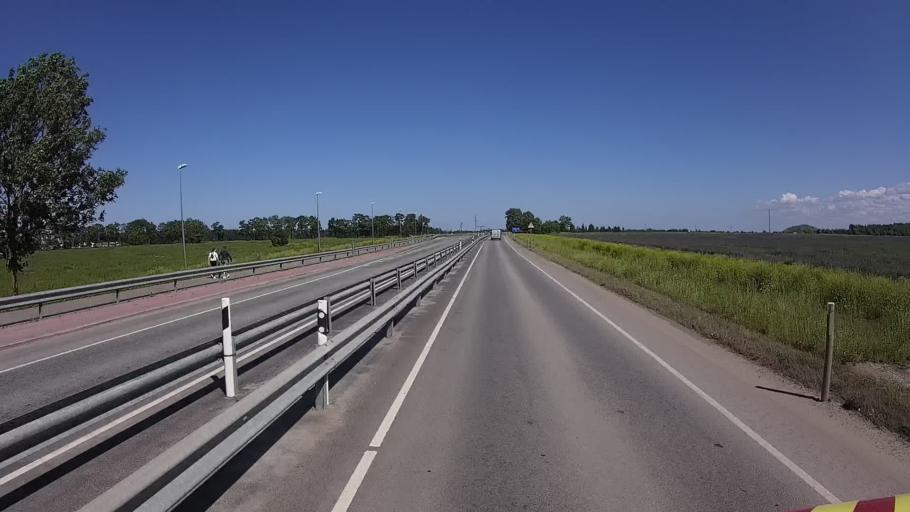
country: EE
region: Ida-Virumaa
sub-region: Kohtla-Jaerve linn
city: Kohtla-Jarve
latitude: 59.4033
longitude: 27.3049
